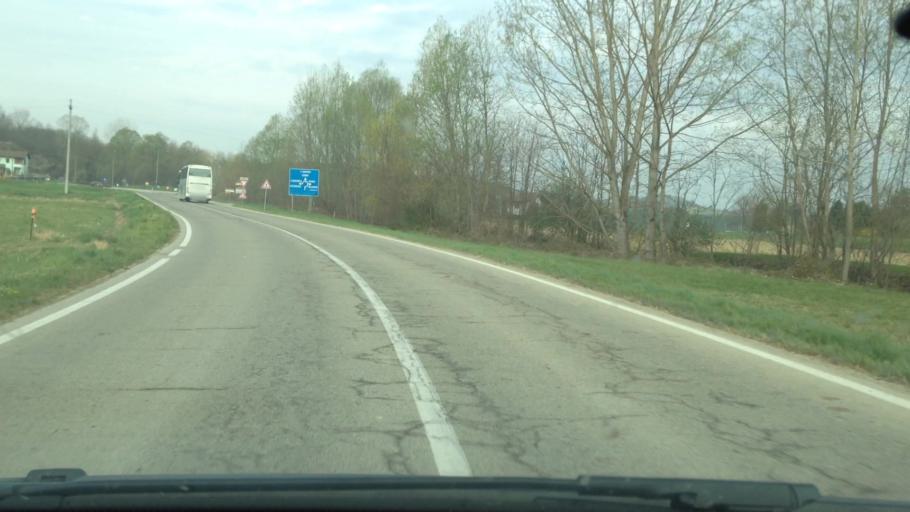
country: IT
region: Piedmont
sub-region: Provincia di Asti
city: San Damiano d'Asti
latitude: 44.8451
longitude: 8.0745
